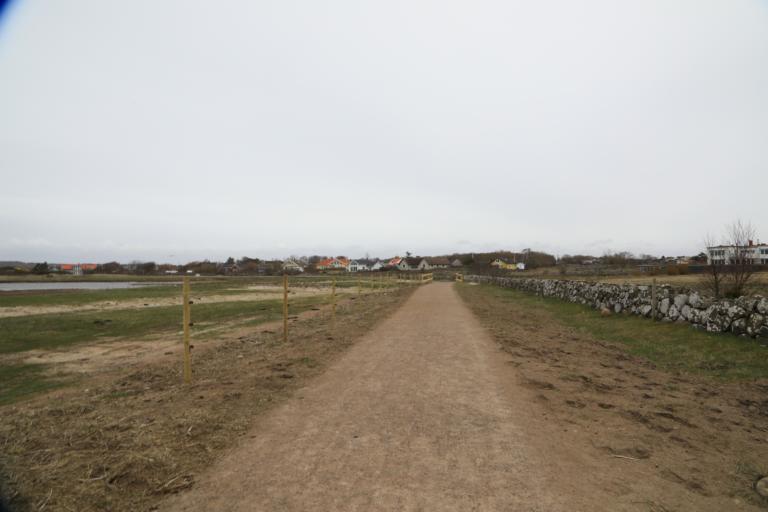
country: SE
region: Halland
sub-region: Varbergs Kommun
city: Traslovslage
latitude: 57.0726
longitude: 12.2593
